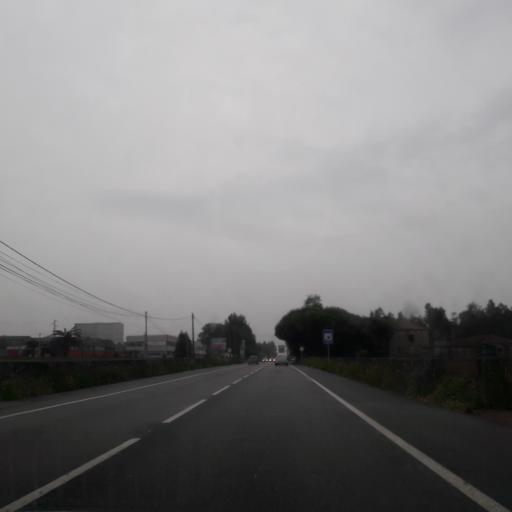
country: PT
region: Porto
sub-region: Vila do Conde
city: Arvore
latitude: 41.3108
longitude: -8.7062
